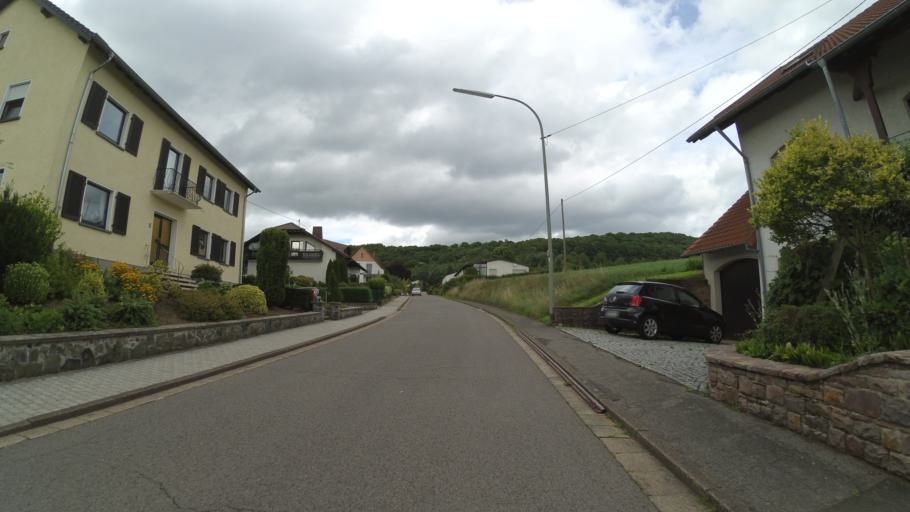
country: DE
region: Saarland
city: Tholey
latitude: 49.4712
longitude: 7.0015
